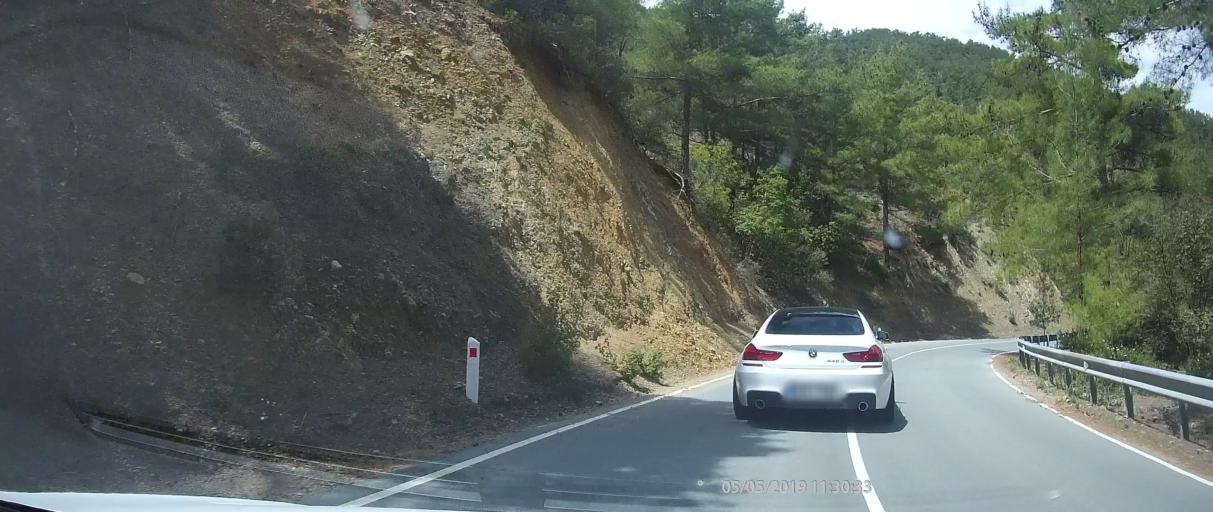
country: CY
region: Limassol
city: Pachna
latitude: 34.9453
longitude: 32.6469
